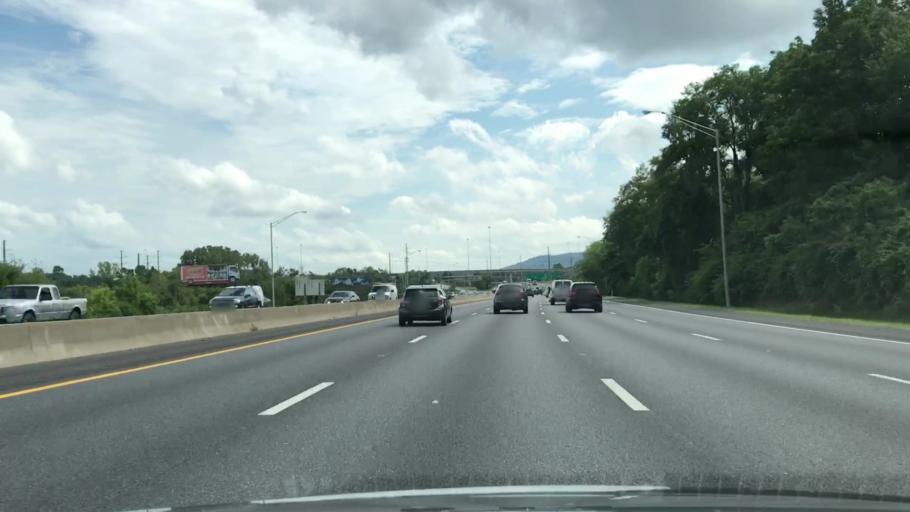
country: US
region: Tennessee
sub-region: Davidson County
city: Oak Hill
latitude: 36.1253
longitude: -86.7719
